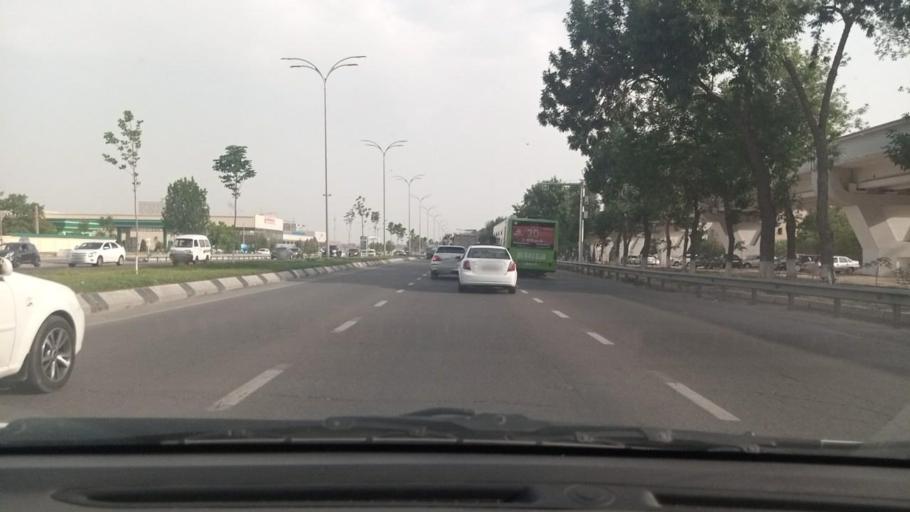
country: UZ
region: Toshkent Shahri
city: Bektemir
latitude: 41.2849
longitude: 69.3602
